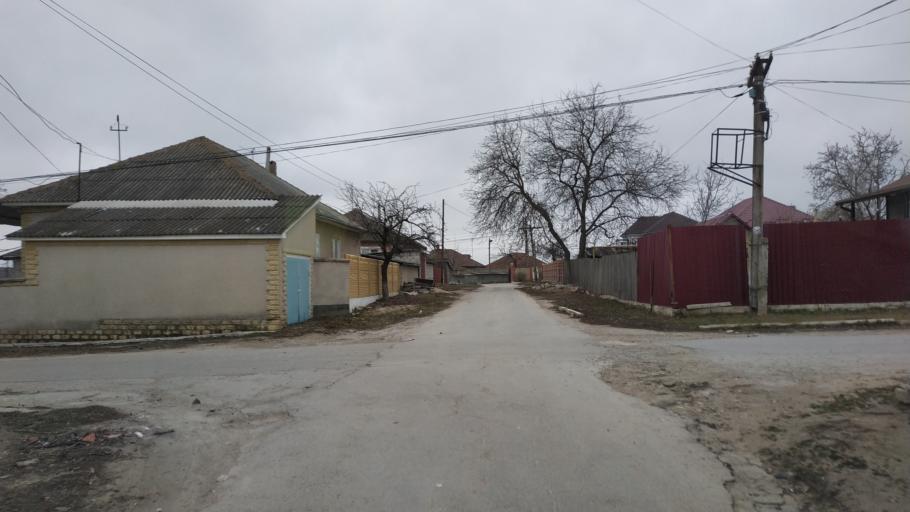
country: MD
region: Laloveni
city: Ialoveni
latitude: 46.9060
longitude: 28.7941
